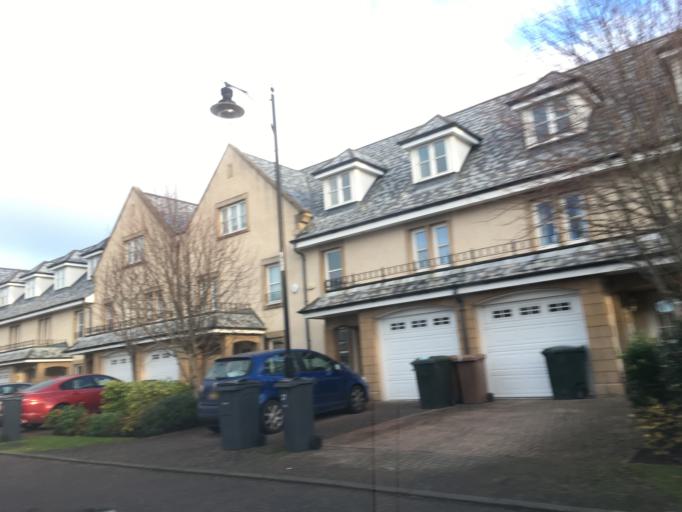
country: GB
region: Scotland
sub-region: Edinburgh
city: Colinton
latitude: 55.9153
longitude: -3.2249
